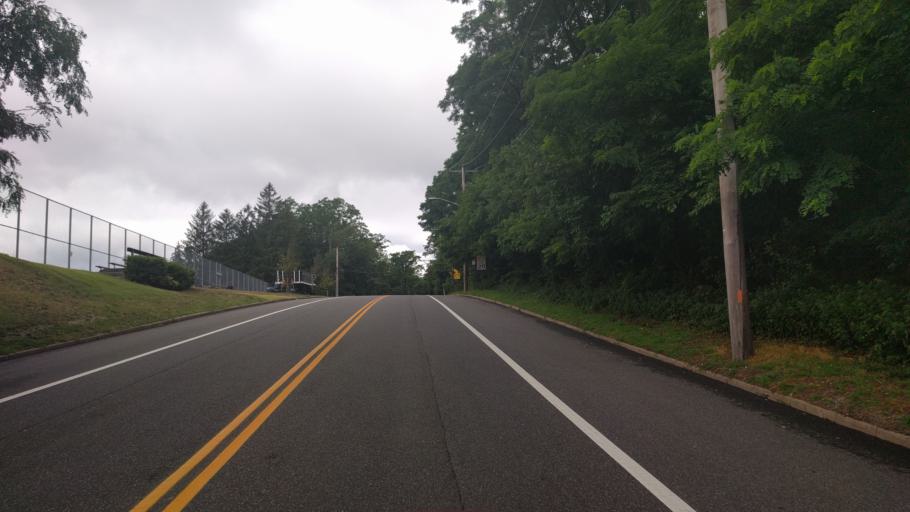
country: US
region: New York
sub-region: Suffolk County
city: Huntington
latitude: 40.8584
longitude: -73.4233
